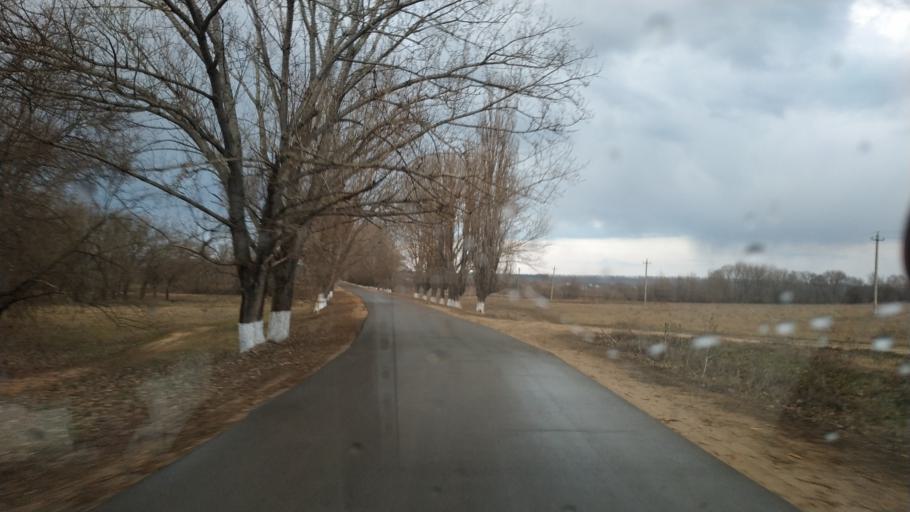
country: MD
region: Telenesti
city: Grigoriopol
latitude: 47.0800
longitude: 29.3293
